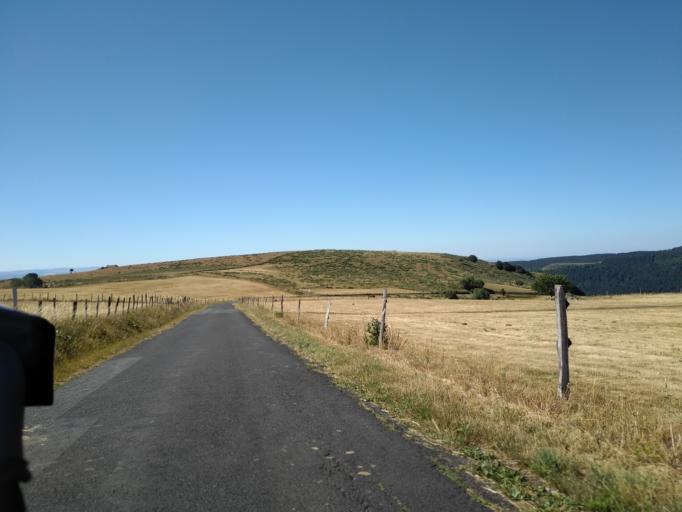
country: FR
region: Auvergne
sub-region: Departement du Cantal
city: Pierrefort
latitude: 45.0142
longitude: 2.8172
